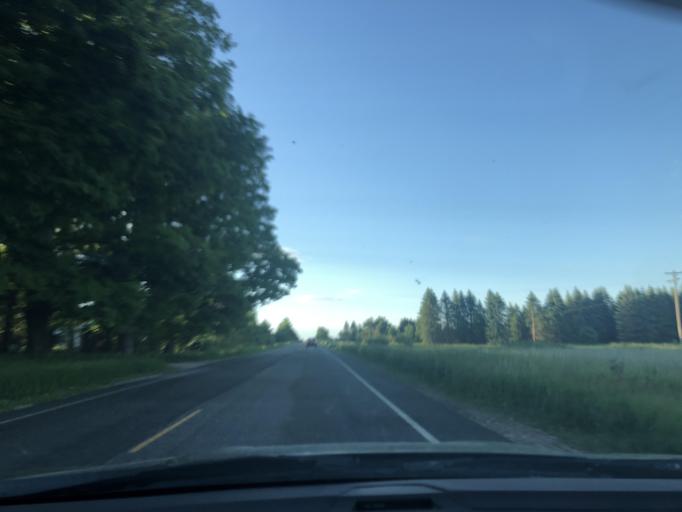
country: US
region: Michigan
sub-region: Missaukee County
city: Lake City
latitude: 44.3995
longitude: -85.0756
